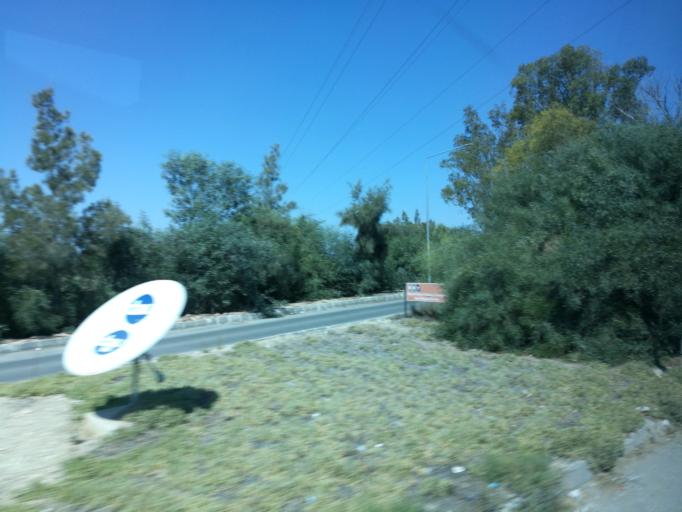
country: CY
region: Ammochostos
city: Famagusta
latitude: 35.1383
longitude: 33.9110
